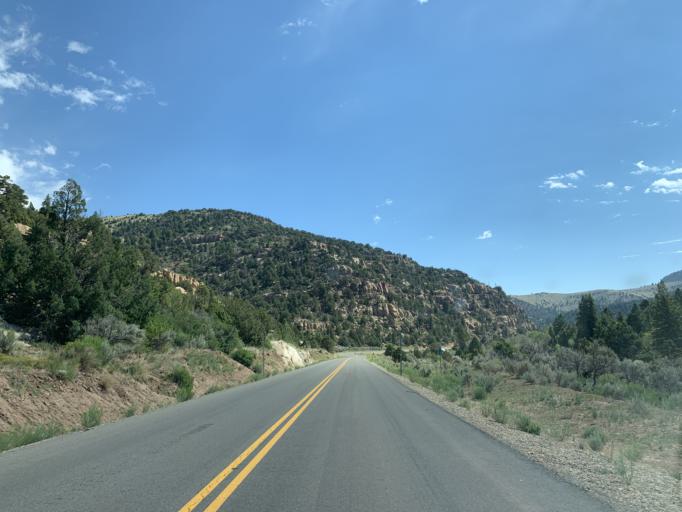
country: US
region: Utah
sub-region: Carbon County
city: East Carbon City
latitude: 39.7524
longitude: -110.5454
